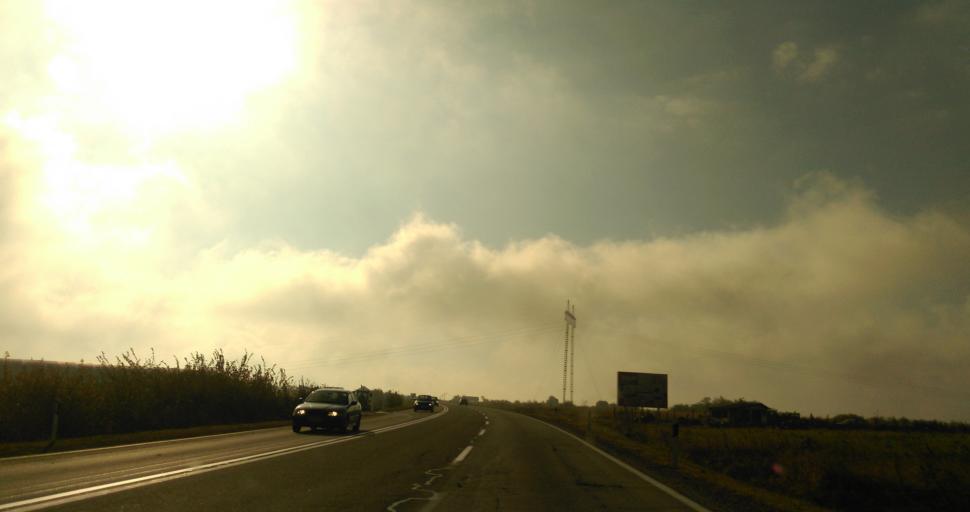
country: RS
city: Rusanj
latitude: 44.6899
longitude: 20.4213
